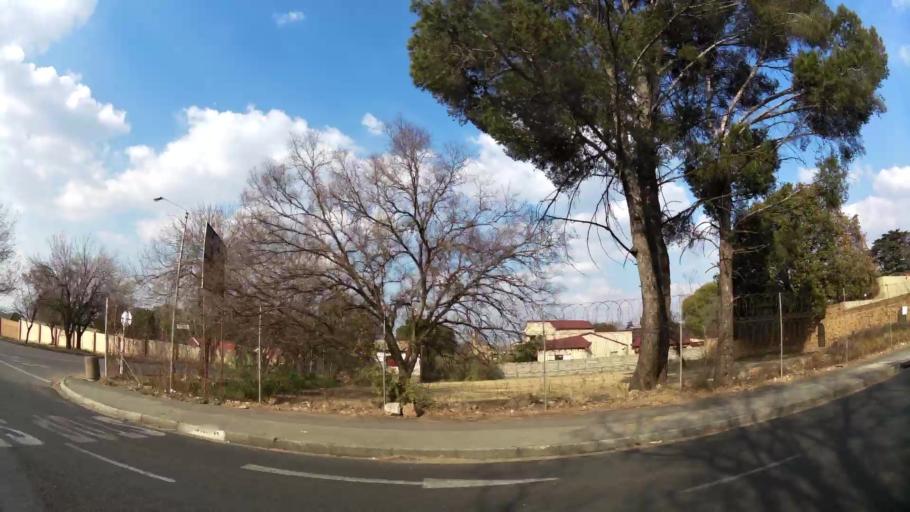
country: ZA
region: Gauteng
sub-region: Ekurhuleni Metropolitan Municipality
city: Germiston
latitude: -26.2369
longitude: 28.1850
